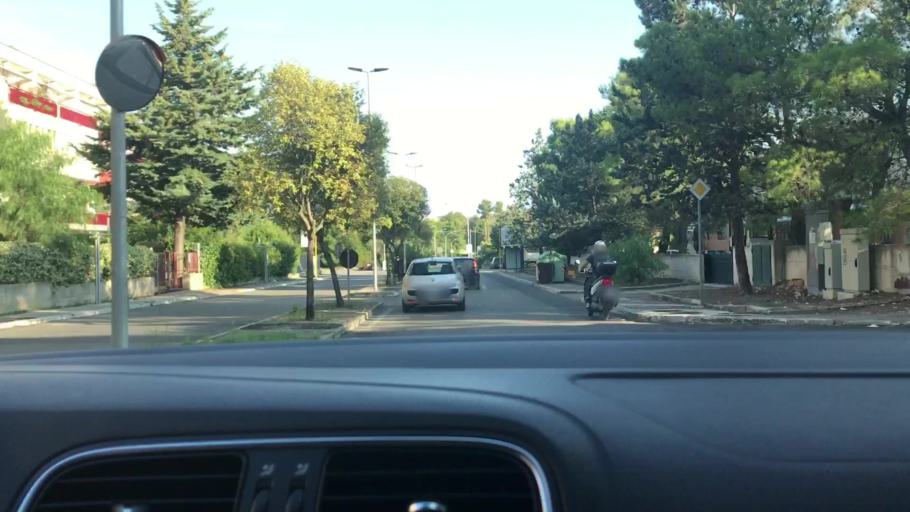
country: IT
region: Basilicate
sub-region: Provincia di Matera
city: Matera
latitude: 40.6819
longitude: 16.5867
